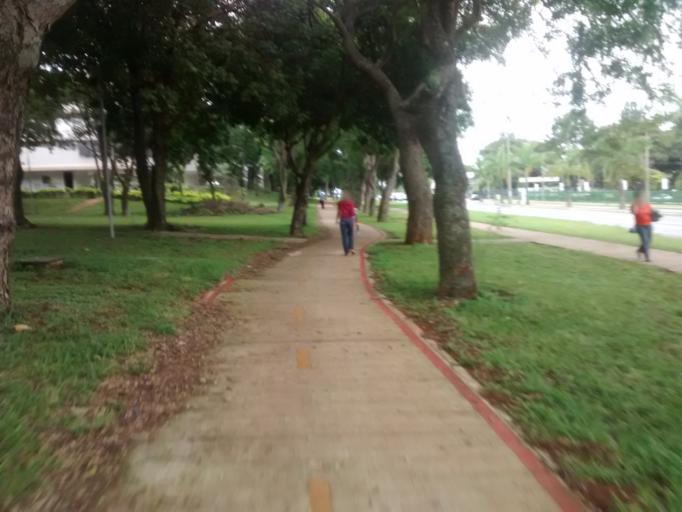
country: BR
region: Federal District
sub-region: Brasilia
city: Brasilia
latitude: -15.7779
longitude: -47.8745
